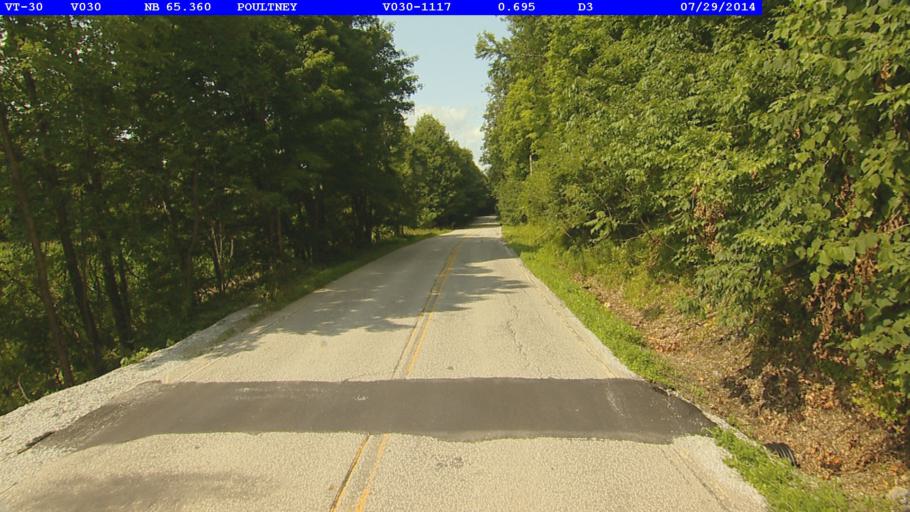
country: US
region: Vermont
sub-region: Rutland County
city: Poultney
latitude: 43.4738
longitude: -73.2022
